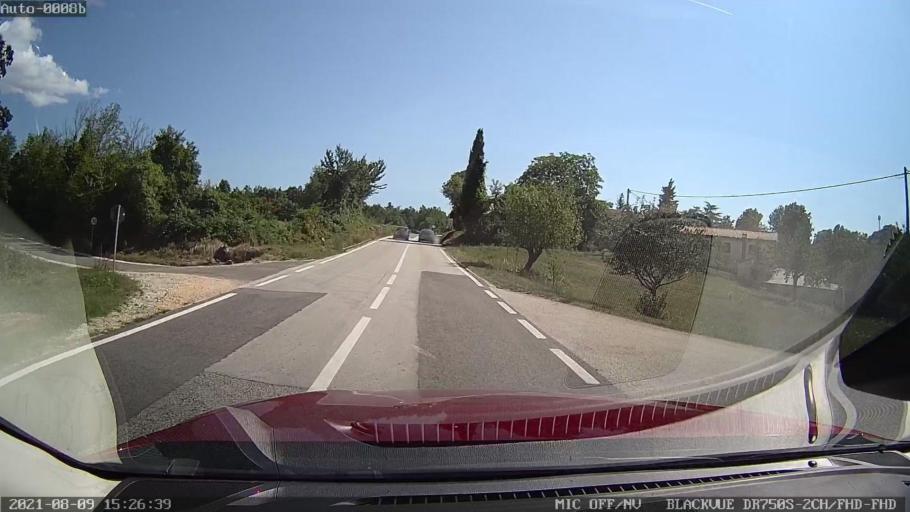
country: HR
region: Istarska
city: Pazin
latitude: 45.1603
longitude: 13.9074
